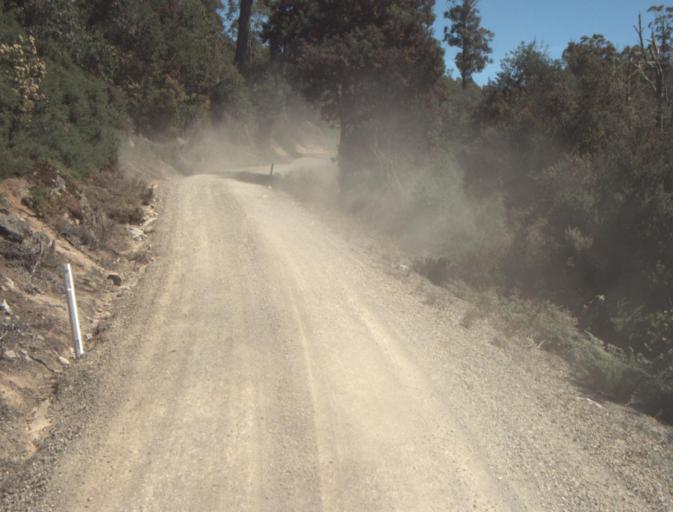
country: AU
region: Tasmania
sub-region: Dorset
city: Scottsdale
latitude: -41.3174
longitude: 147.4639
